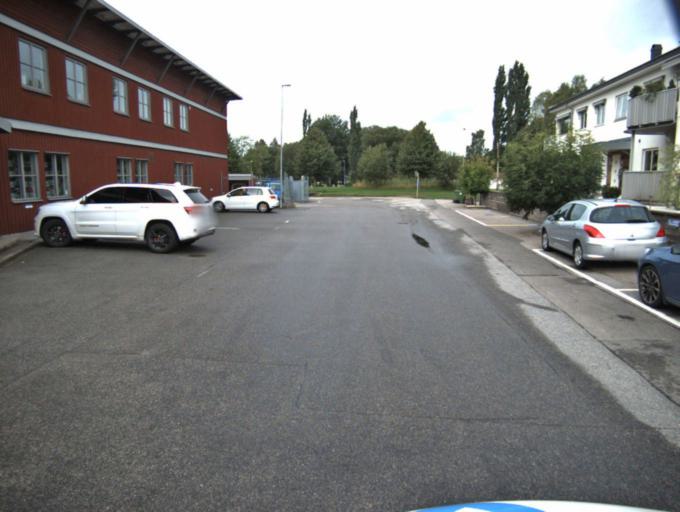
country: SE
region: Vaestra Goetaland
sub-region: Ulricehamns Kommun
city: Ulricehamn
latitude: 57.7990
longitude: 13.4128
